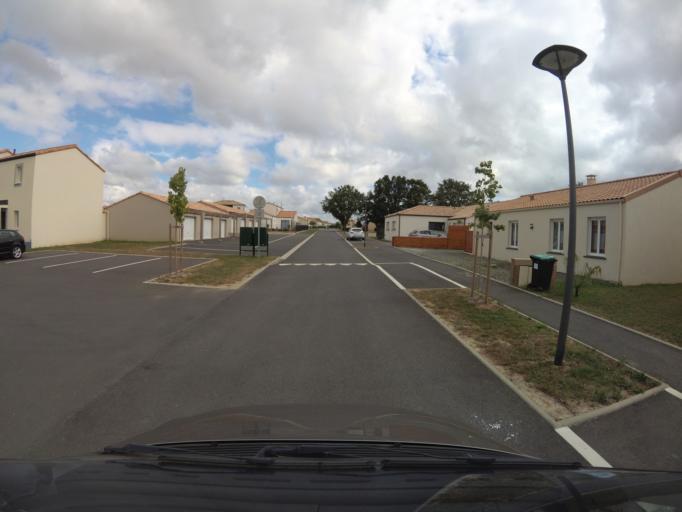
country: FR
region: Pays de la Loire
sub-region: Departement de la Vendee
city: Saint-Philbert-de-Bouaine
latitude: 46.9948
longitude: -1.5237
